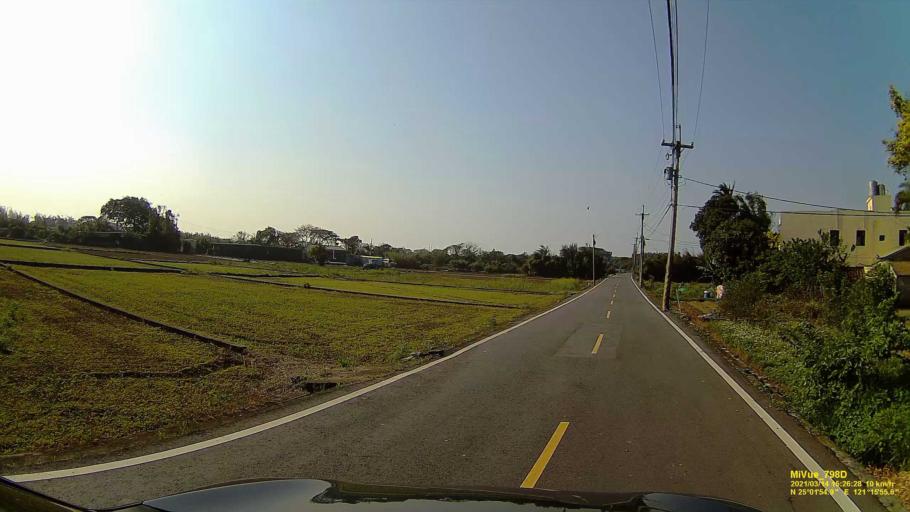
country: TW
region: Taiwan
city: Taoyuan City
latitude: 25.0319
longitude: 121.2654
